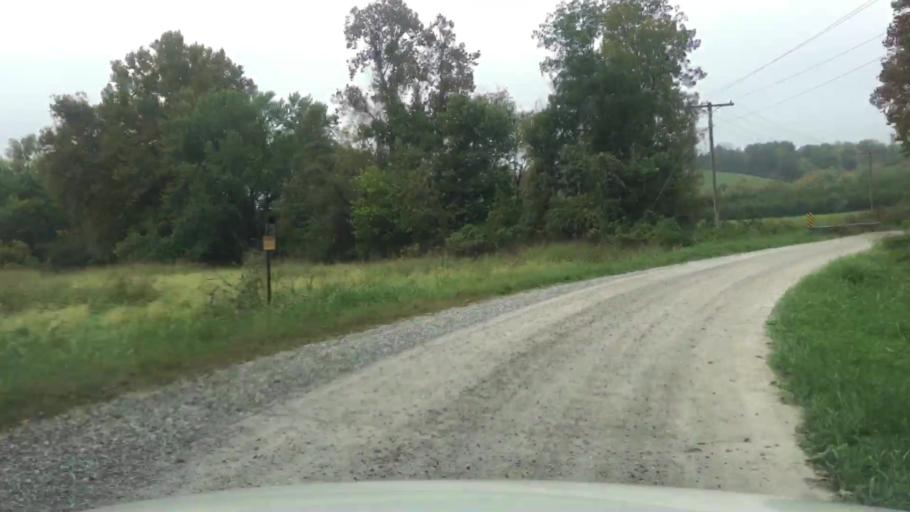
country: US
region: Missouri
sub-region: Boone County
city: Ashland
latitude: 38.8210
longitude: -92.3421
